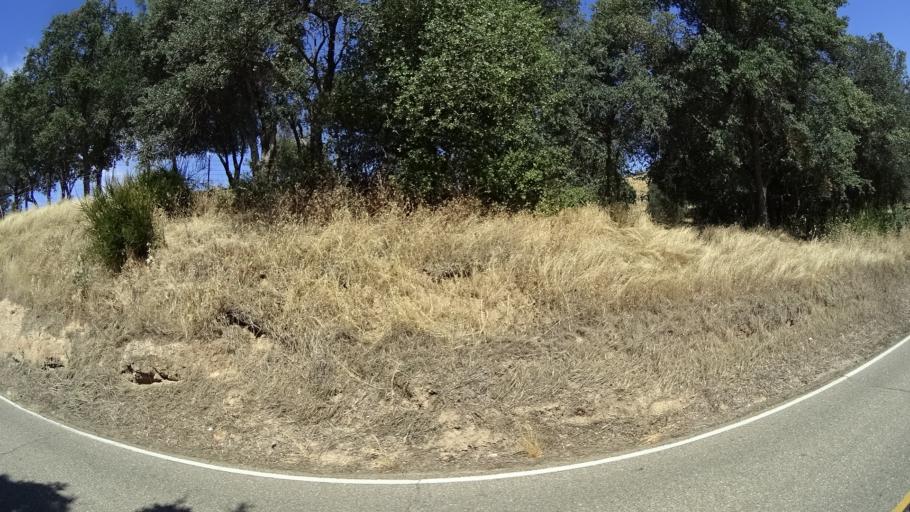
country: US
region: California
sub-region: Calaveras County
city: Rancho Calaveras
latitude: 38.1496
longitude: -120.8965
